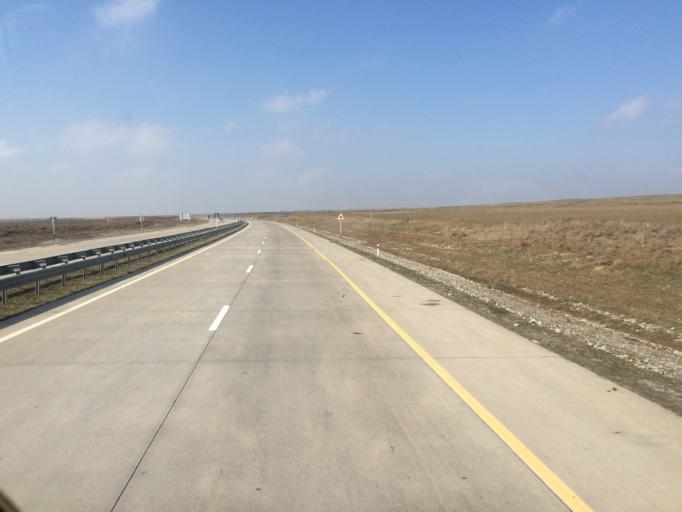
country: KZ
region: Ongtustik Qazaqstan
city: Shymkent
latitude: 42.4892
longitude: 69.5166
